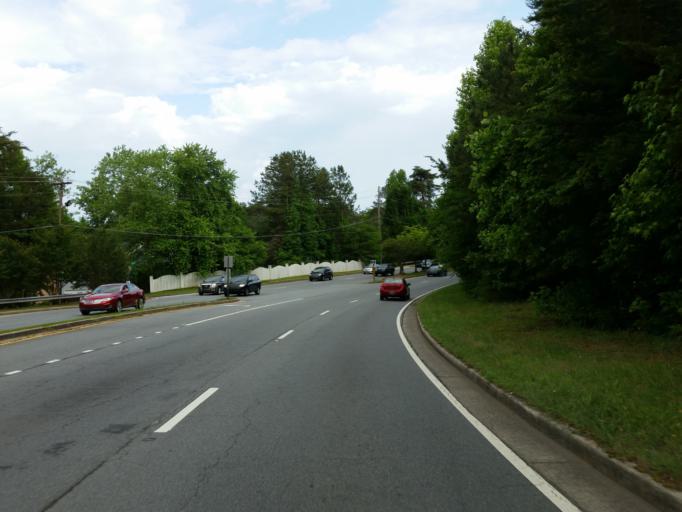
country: US
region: Georgia
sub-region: Cobb County
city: Marietta
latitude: 33.9858
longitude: -84.4868
